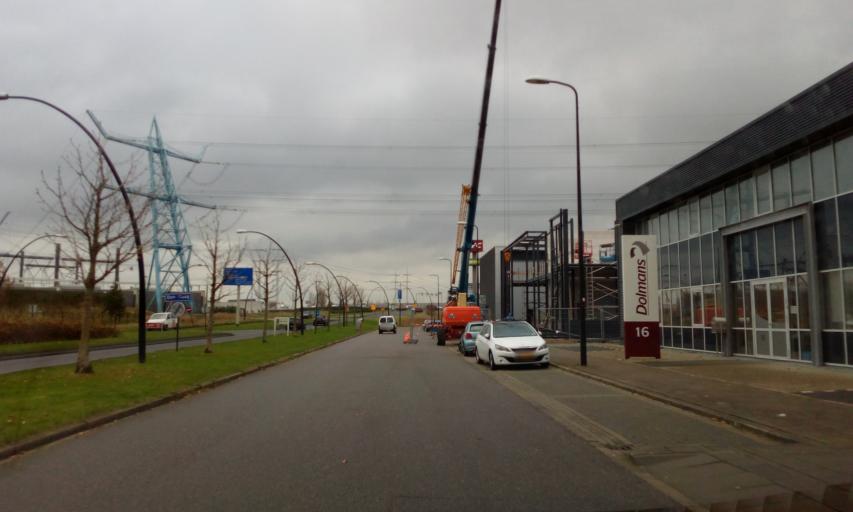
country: NL
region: South Holland
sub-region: Gemeente Rijswijk
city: Rijswijk
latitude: 52.0171
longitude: 4.3032
